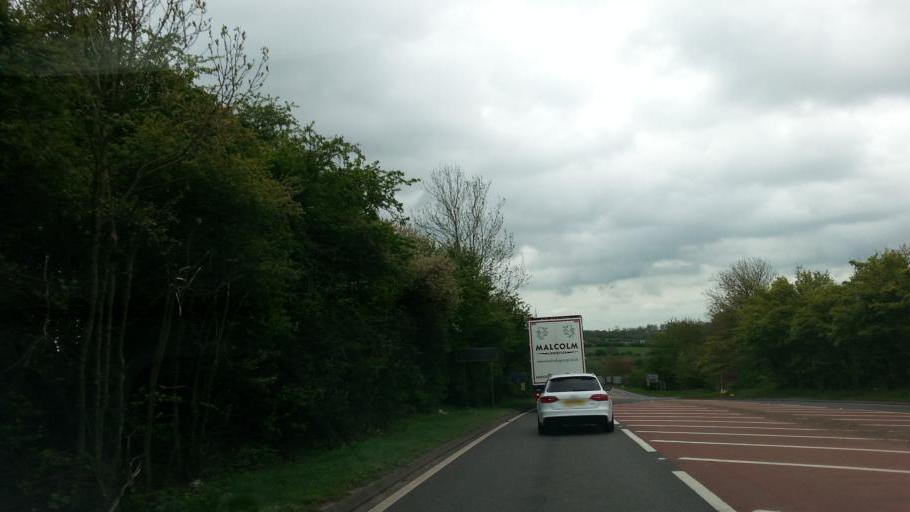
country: GB
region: England
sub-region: Leicestershire
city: Lutterworth
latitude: 52.4002
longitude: -1.2058
